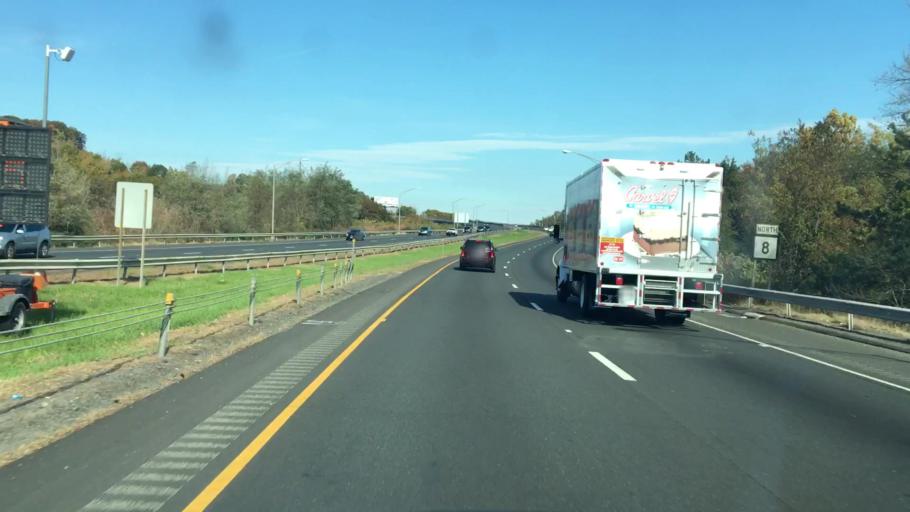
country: US
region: Connecticut
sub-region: New Haven County
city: Naugatuck
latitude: 41.5206
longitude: -73.0470
